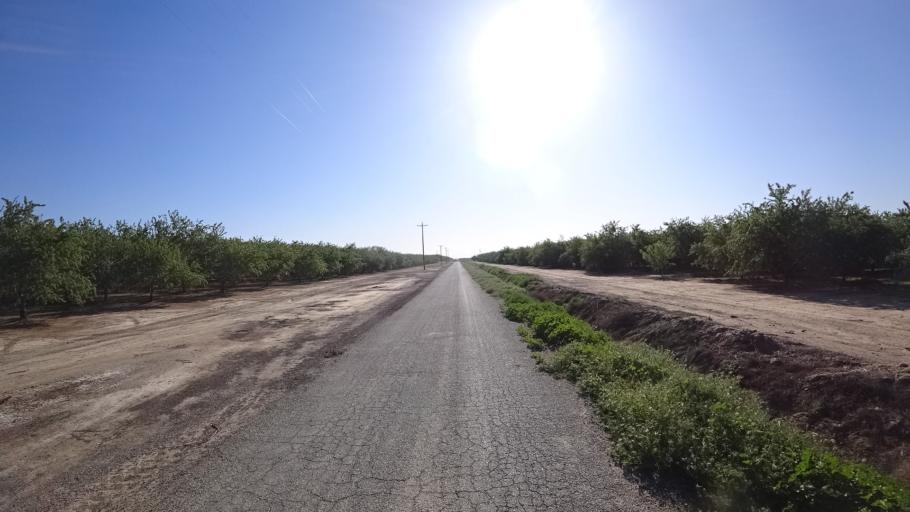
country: US
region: California
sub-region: Glenn County
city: Hamilton City
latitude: 39.6948
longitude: -122.0586
